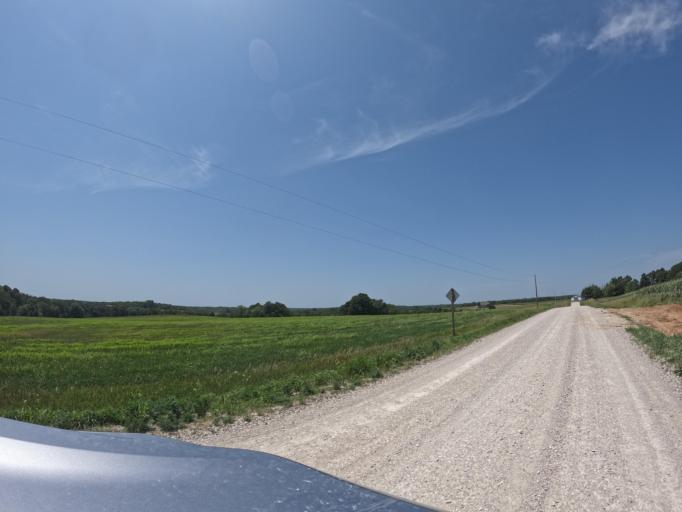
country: US
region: Iowa
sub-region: Henry County
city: Mount Pleasant
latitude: 40.9127
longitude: -91.6567
